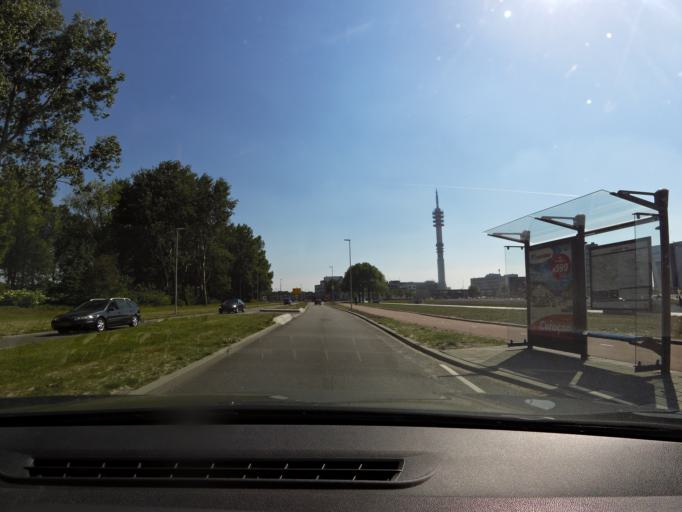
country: NL
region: South Holland
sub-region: Gemeente Rotterdam
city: Delfshaven
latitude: 51.8802
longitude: 4.4542
